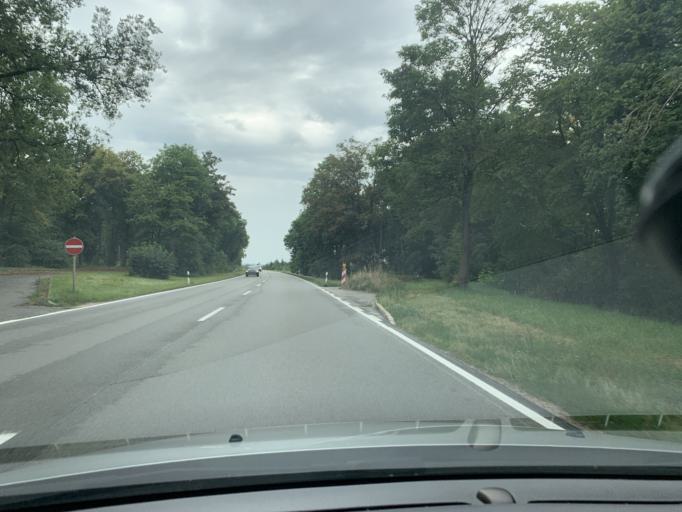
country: DE
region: Bavaria
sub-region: Upper Bavaria
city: Neufahrn
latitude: 48.2518
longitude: 12.4539
